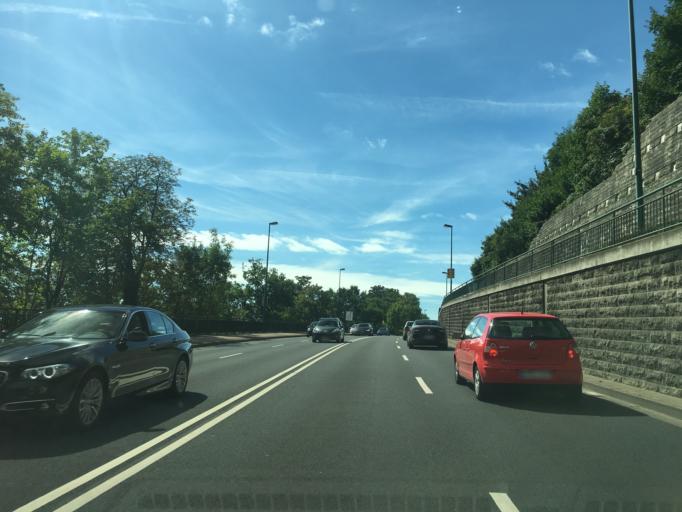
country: DE
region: Lower Saxony
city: Hameln
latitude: 52.0935
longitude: 9.3522
